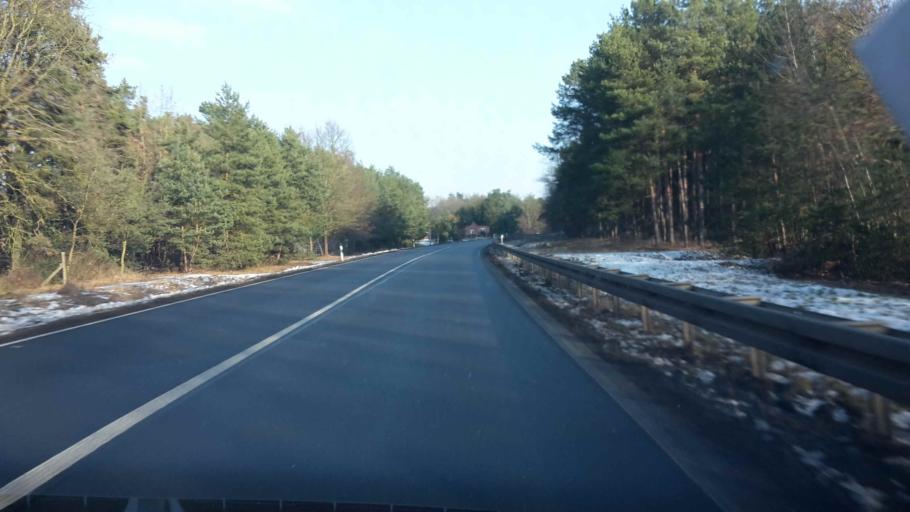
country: DE
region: Brandenburg
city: Wittenberge
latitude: 53.0208
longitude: 11.7468
